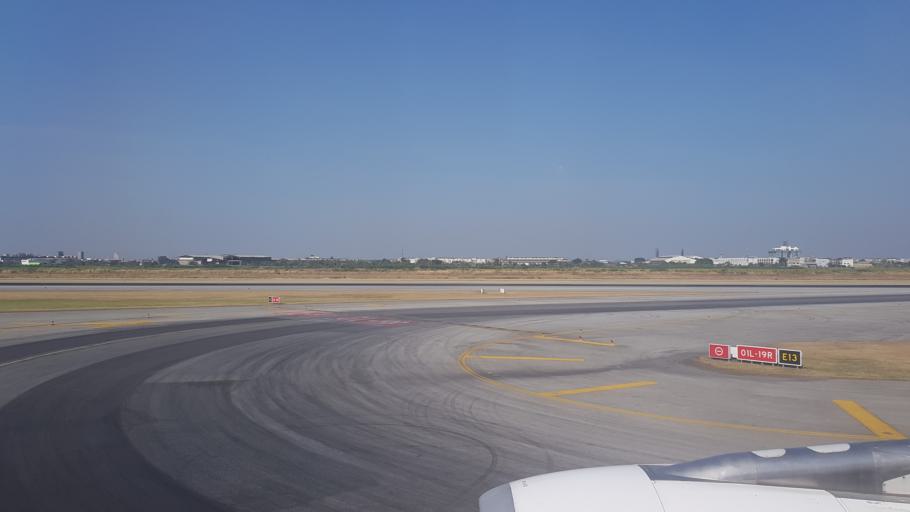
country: TH
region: Bangkok
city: Lat Krabang
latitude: 13.6823
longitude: 100.7395
